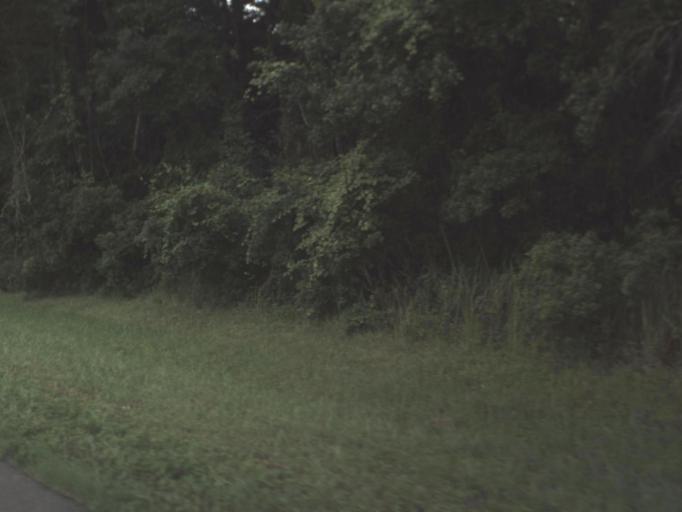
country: US
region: Florida
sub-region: Hillsborough County
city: Wimauma
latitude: 27.7057
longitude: -82.2596
